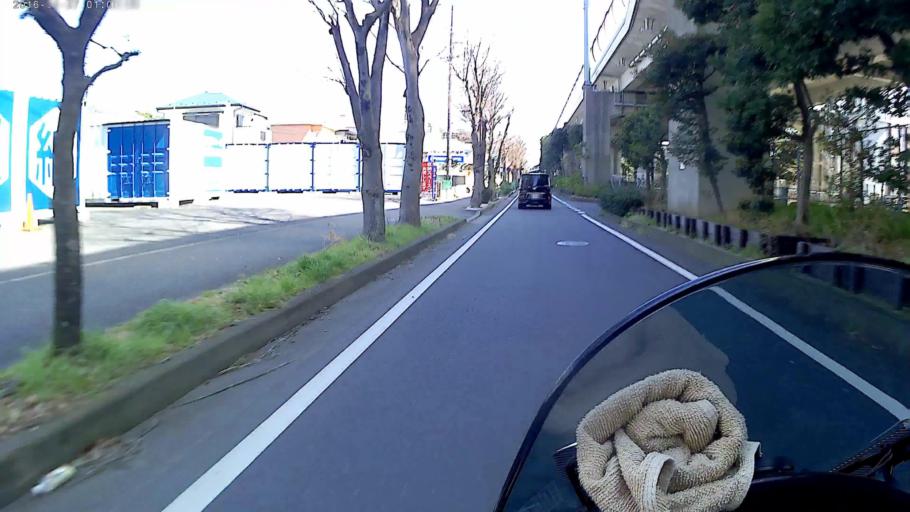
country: JP
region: Kanagawa
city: Chigasaki
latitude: 35.3493
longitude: 139.4185
